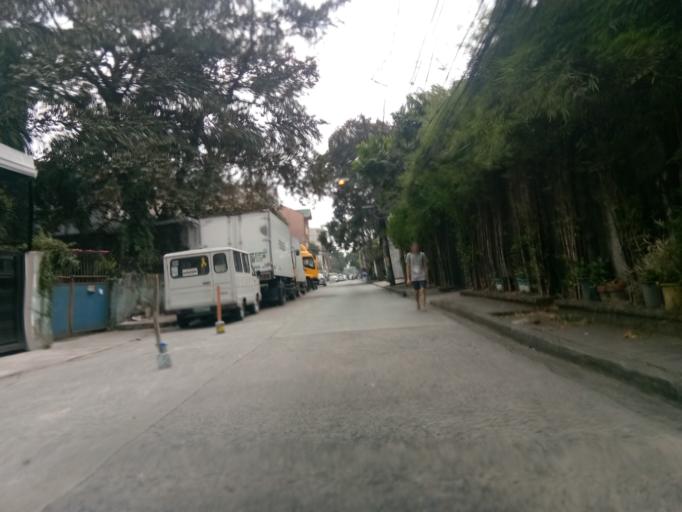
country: PH
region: Metro Manila
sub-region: San Juan
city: San Juan
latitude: 14.6165
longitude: 121.0554
